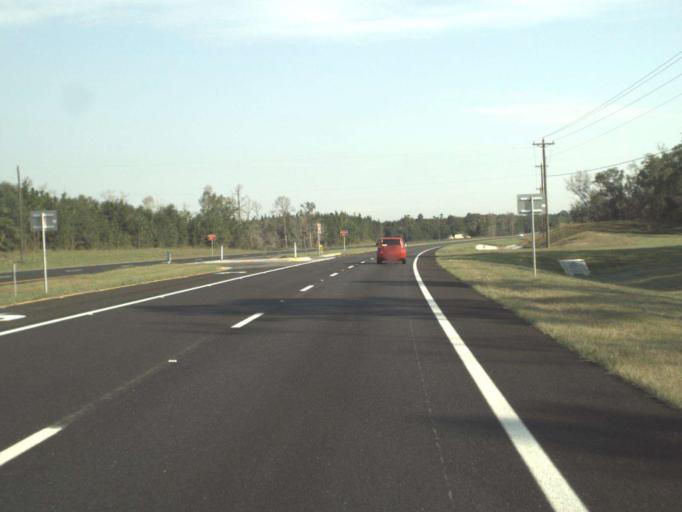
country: US
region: Florida
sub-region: Bay County
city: Laguna Beach
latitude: 30.5168
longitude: -85.8419
